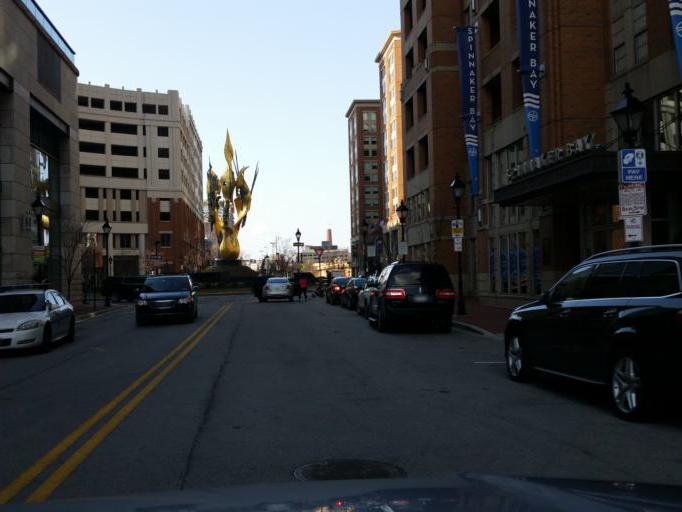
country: US
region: Maryland
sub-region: City of Baltimore
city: Baltimore
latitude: 39.2826
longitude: -76.6011
